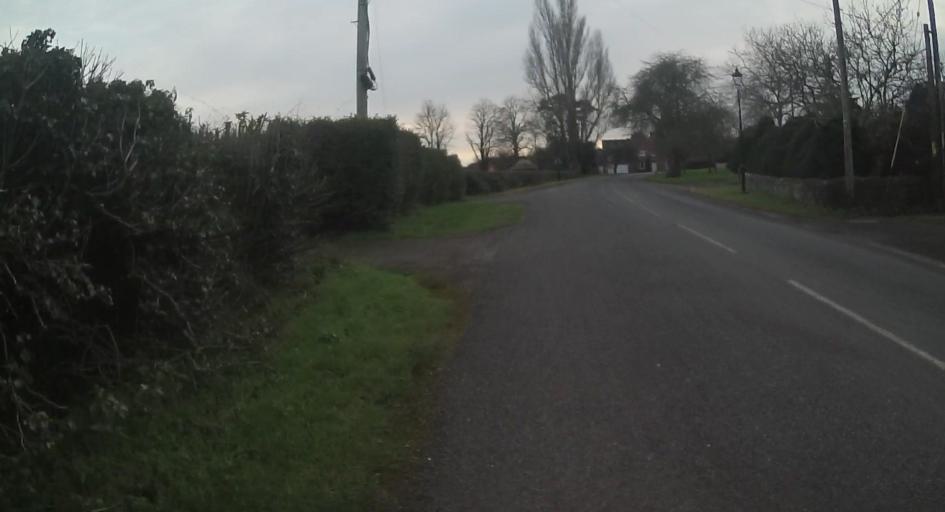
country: GB
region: England
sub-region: Hampshire
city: Overton
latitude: 51.2164
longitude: -1.3743
